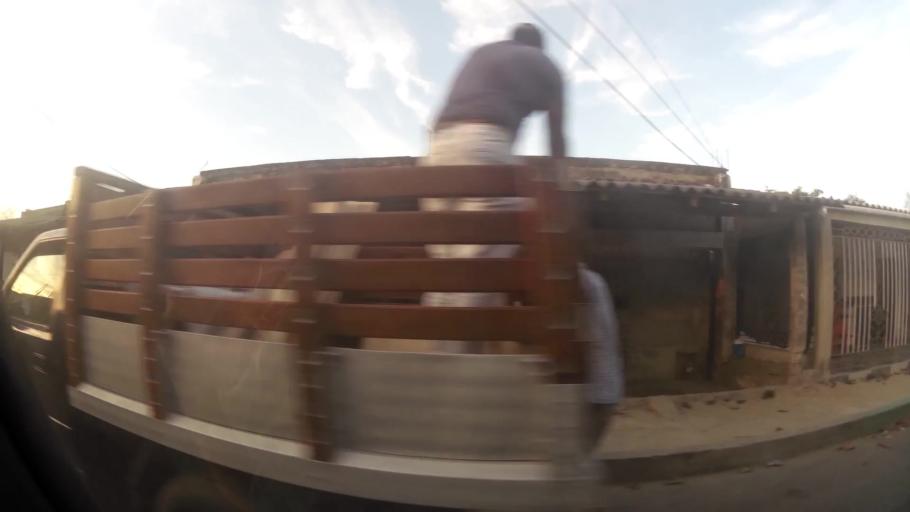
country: CO
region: Atlantico
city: Barranquilla
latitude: 10.9551
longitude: -74.8225
